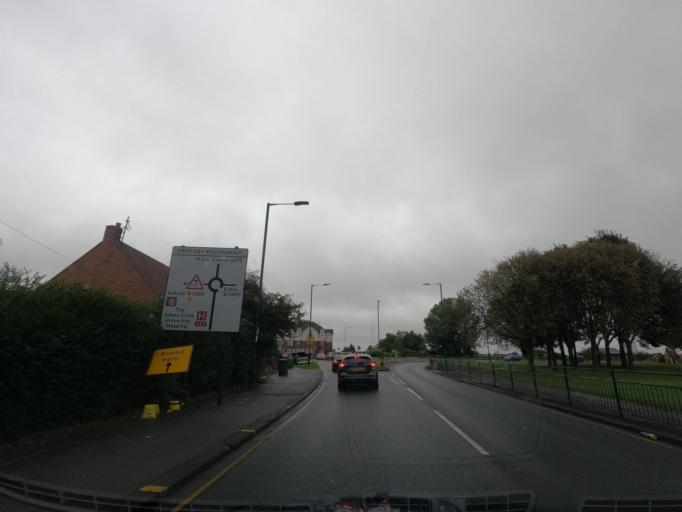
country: GB
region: England
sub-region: Middlesbrough
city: Nunthorpe
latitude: 54.5494
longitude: -1.1796
